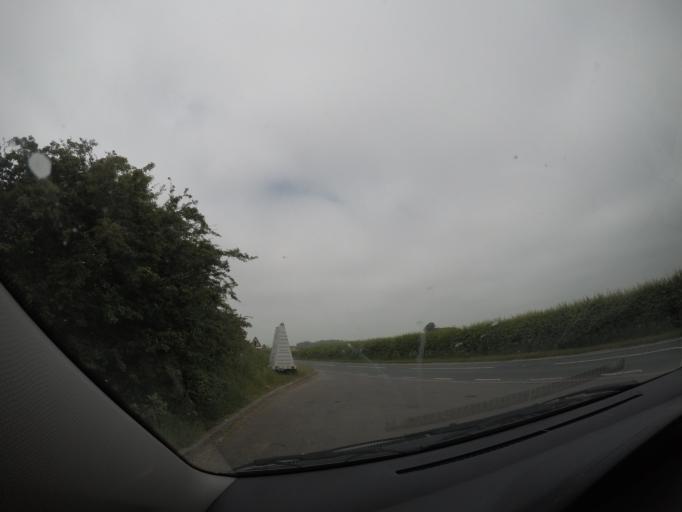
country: GB
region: England
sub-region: City and Borough of Leeds
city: Wetherby
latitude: 54.0080
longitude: -1.3530
